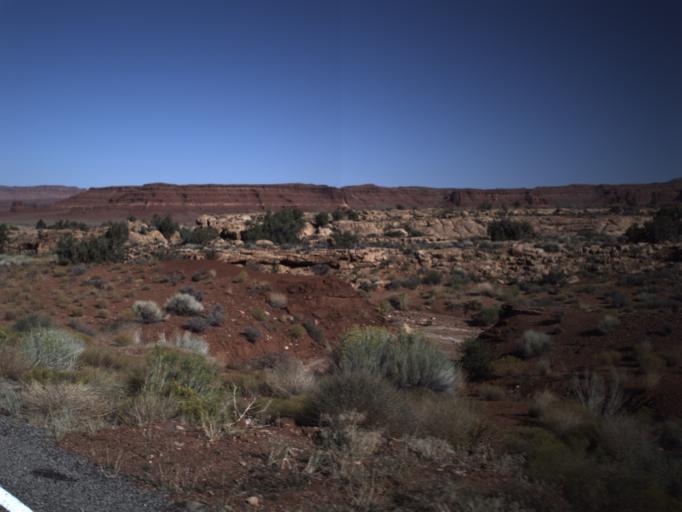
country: US
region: Utah
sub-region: San Juan County
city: Blanding
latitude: 37.8083
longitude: -110.3268
